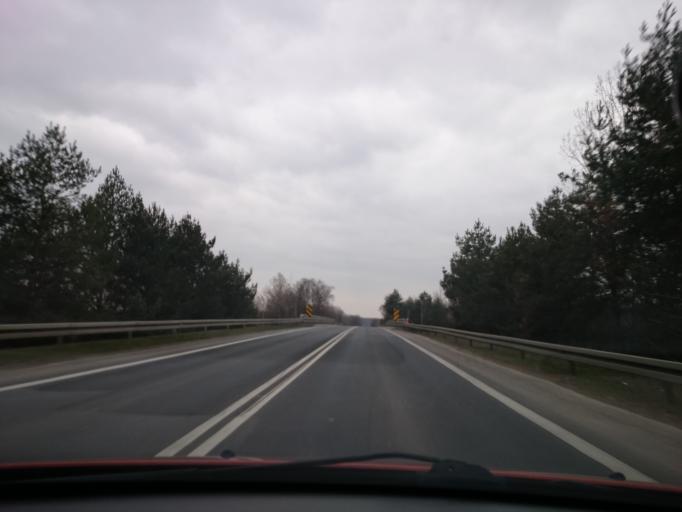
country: PL
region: Opole Voivodeship
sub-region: Powiat opolski
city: Dabrowa
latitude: 50.6627
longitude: 17.6960
